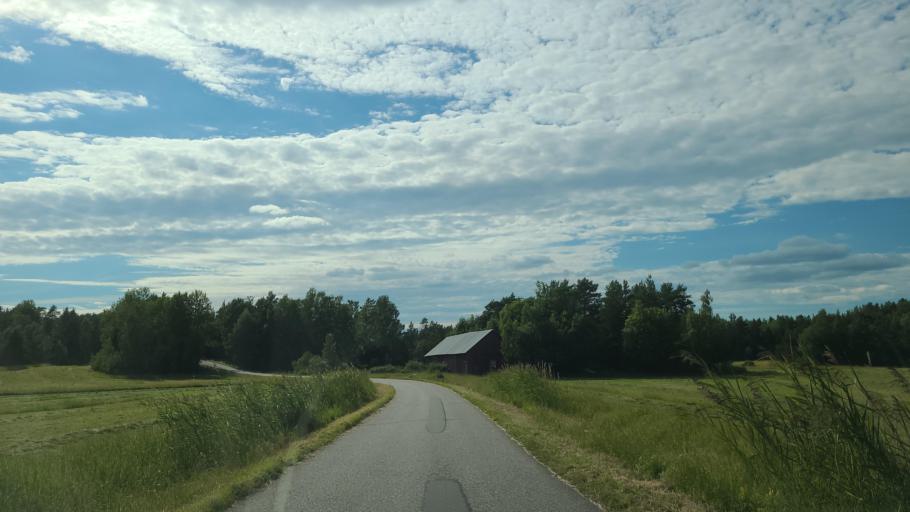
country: FI
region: Varsinais-Suomi
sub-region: Turku
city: Rymaettylae
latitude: 60.2904
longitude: 21.9577
